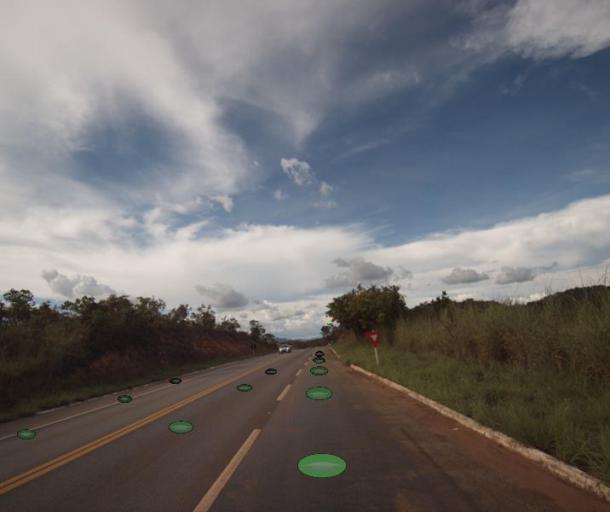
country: BR
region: Goias
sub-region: Barro Alto
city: Barro Alto
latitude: -15.1001
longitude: -48.7483
